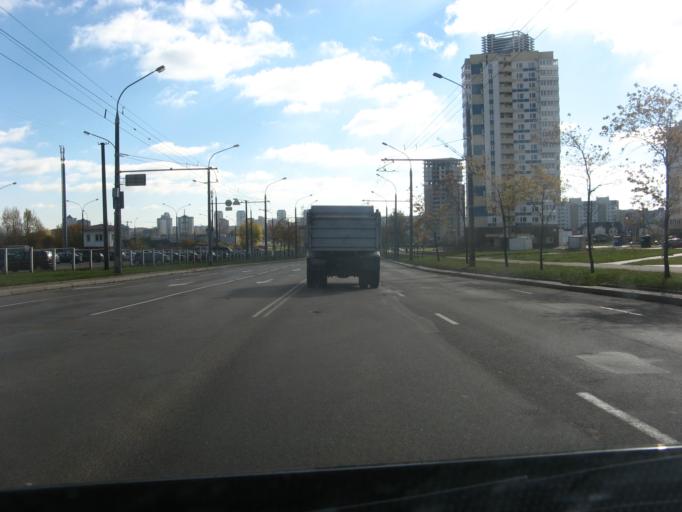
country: BY
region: Minsk
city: Novoye Medvezhino
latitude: 53.8798
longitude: 27.4562
